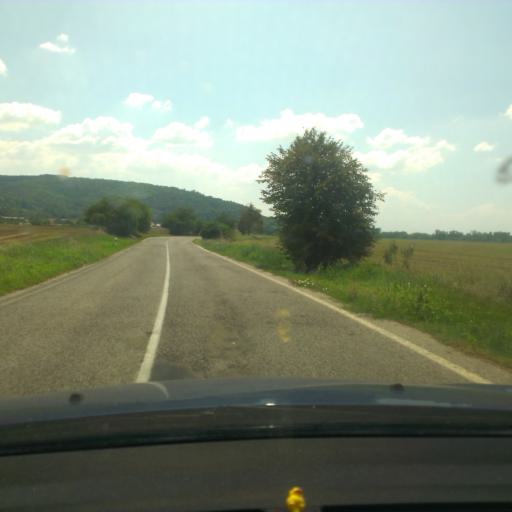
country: SK
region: Trnavsky
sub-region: Okres Trnava
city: Piestany
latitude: 48.5153
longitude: 17.8250
